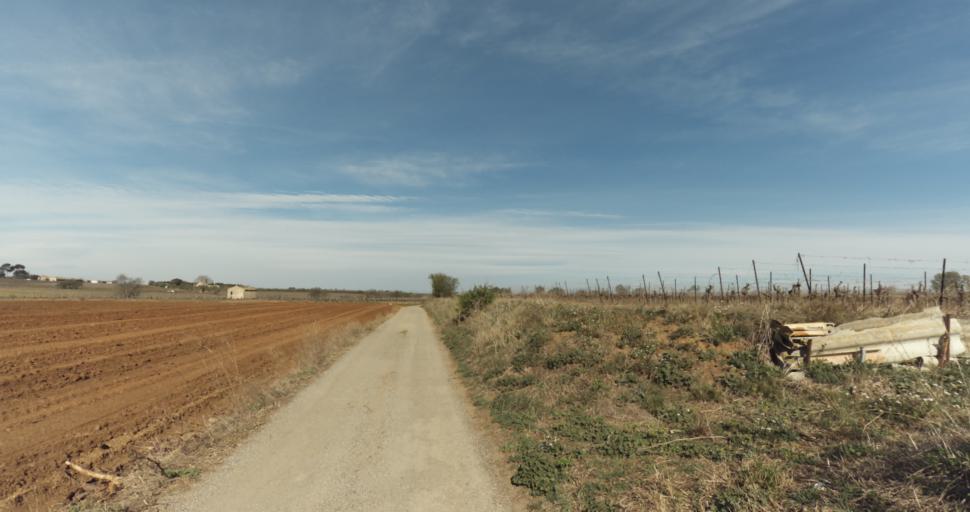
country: FR
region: Languedoc-Roussillon
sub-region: Departement de l'Herault
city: Marseillan
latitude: 43.3514
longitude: 3.4967
